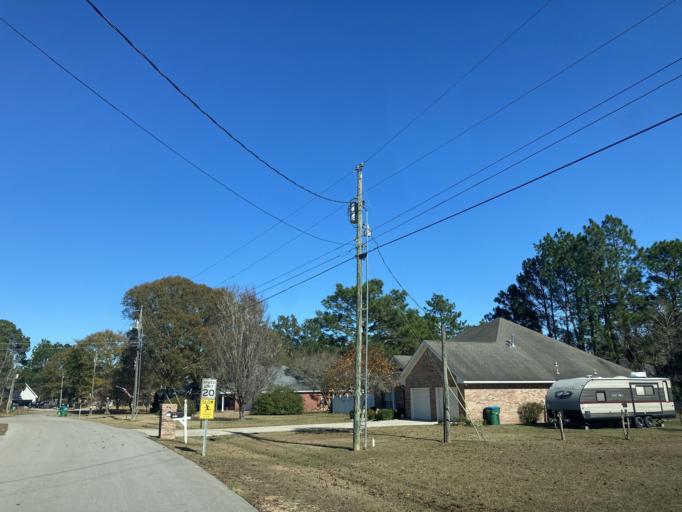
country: US
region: Mississippi
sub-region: Forrest County
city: Petal
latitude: 31.3451
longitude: -89.1858
